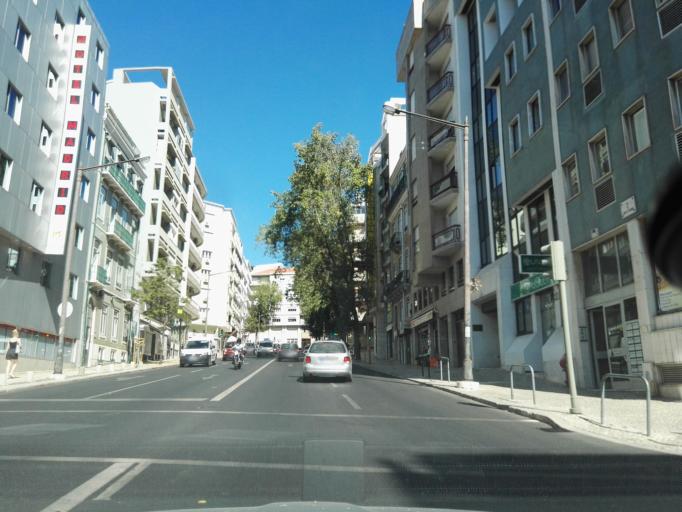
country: PT
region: Lisbon
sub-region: Lisbon
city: Lisbon
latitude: 38.7268
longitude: -9.1446
